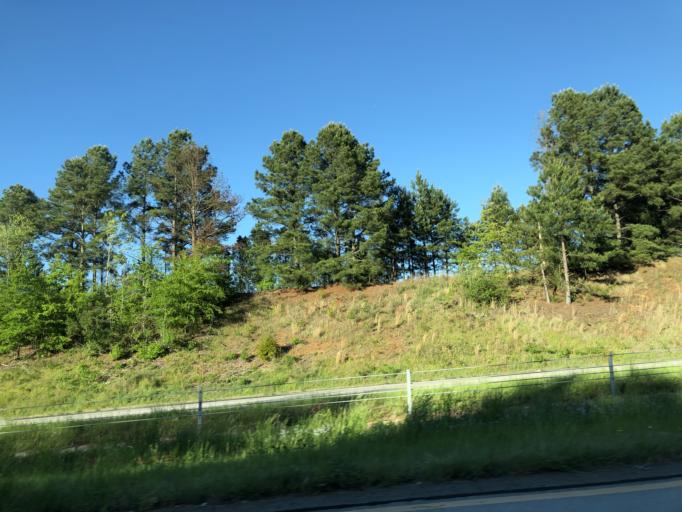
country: US
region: Georgia
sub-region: Oconee County
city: Bogart
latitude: 33.9236
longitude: -83.4642
